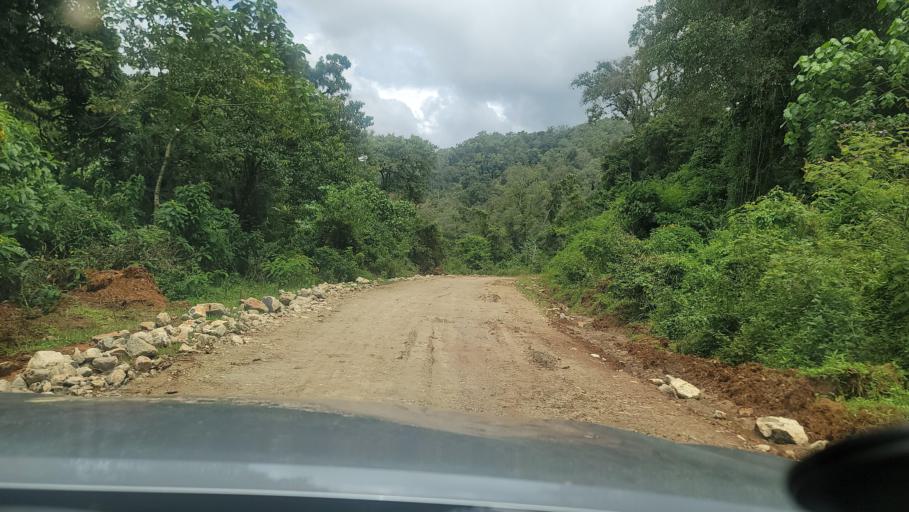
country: ET
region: Southern Nations, Nationalities, and People's Region
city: Bonga
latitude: 7.6159
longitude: 36.2064
